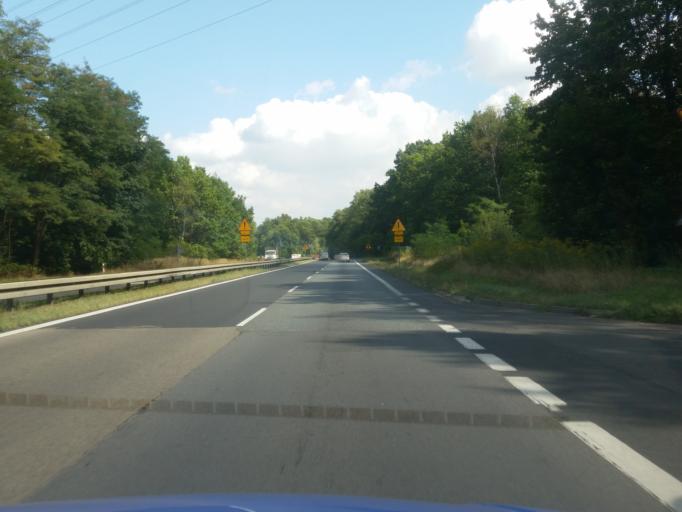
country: PL
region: Silesian Voivodeship
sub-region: Powiat bedzinski
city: Sarnow
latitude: 50.3840
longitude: 19.1759
